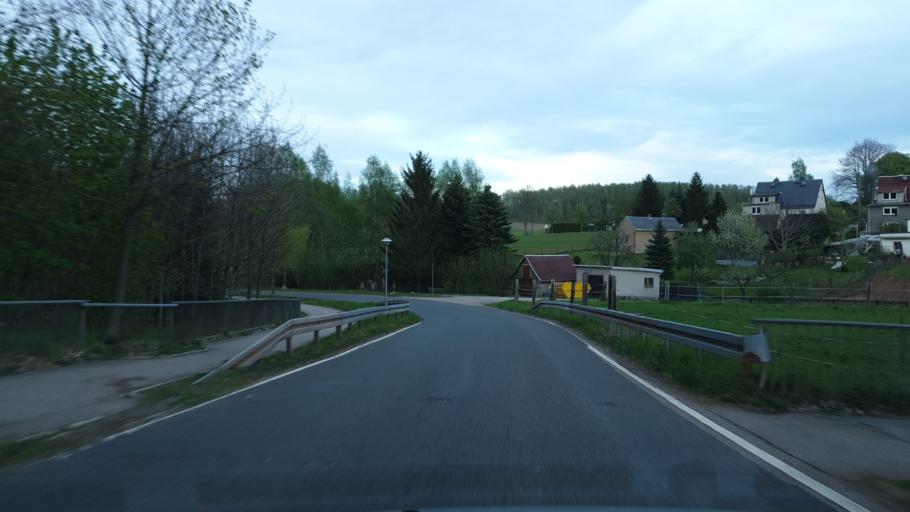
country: DE
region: Saxony
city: Gersdorf
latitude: 50.7377
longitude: 12.7126
